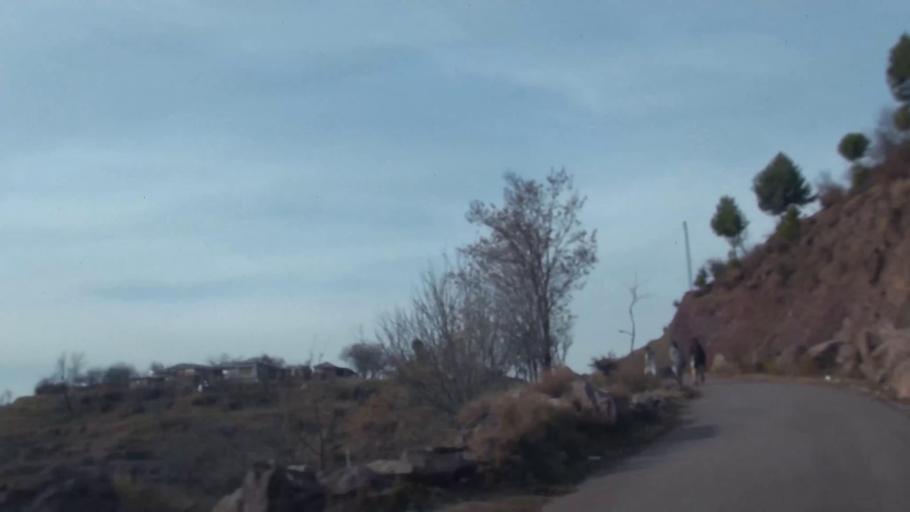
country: PK
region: Azad Kashmir
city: Muzaffarabad
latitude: 34.3688
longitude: 73.5137
